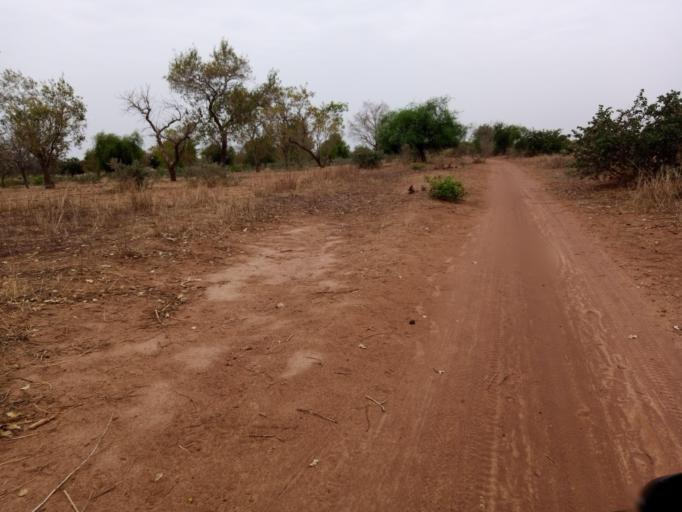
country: BF
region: Boucle du Mouhoun
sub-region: Province de la Kossi
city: Nouna
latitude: 12.8386
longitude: -4.0768
